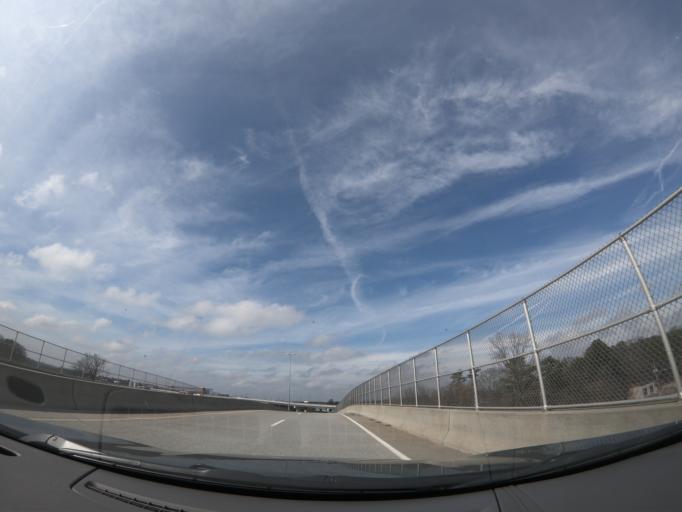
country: US
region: Georgia
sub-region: Fulton County
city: College Park
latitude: 33.6382
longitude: -84.4595
